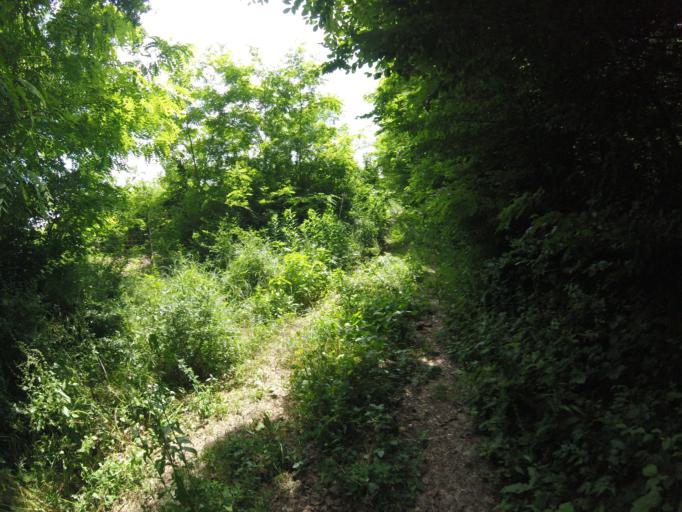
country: HU
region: Zala
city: Turje
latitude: 47.0360
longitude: 17.0410
